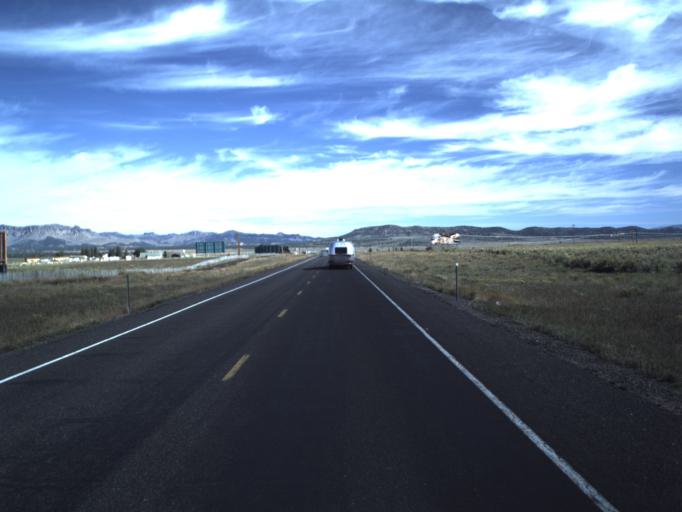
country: US
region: Utah
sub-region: Garfield County
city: Panguitch
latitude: 37.6822
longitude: -112.1543
